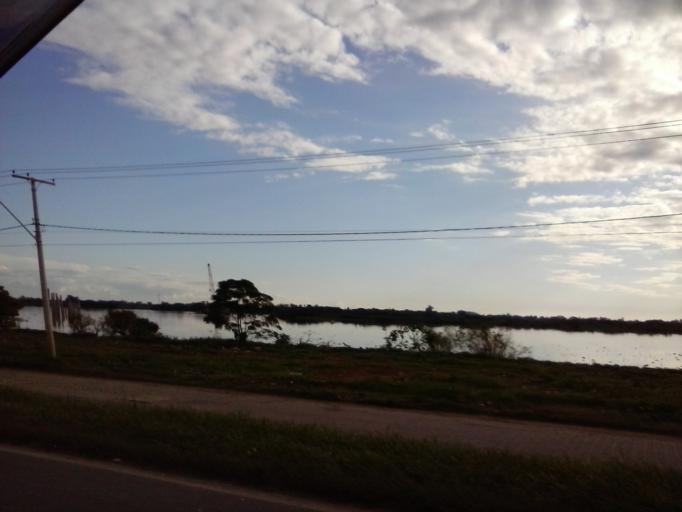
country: BR
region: Rio Grande do Sul
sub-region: Porto Alegre
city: Porto Alegre
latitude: -29.9854
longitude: -51.2028
